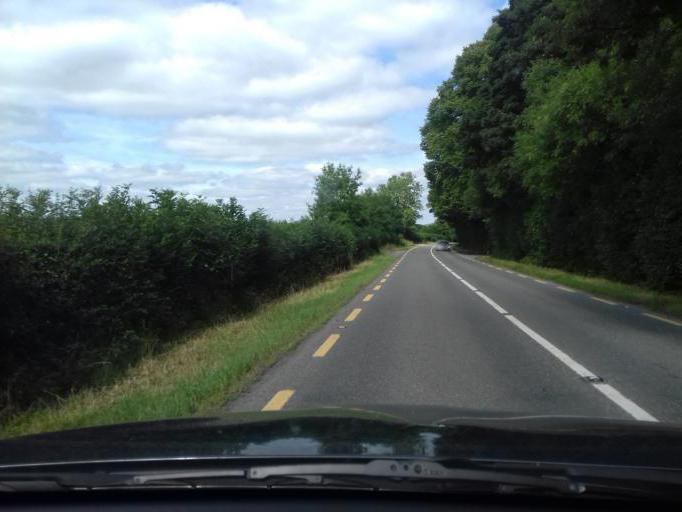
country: IE
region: Leinster
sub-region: Wicklow
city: Baltinglass
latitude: 52.9909
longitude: -6.6548
